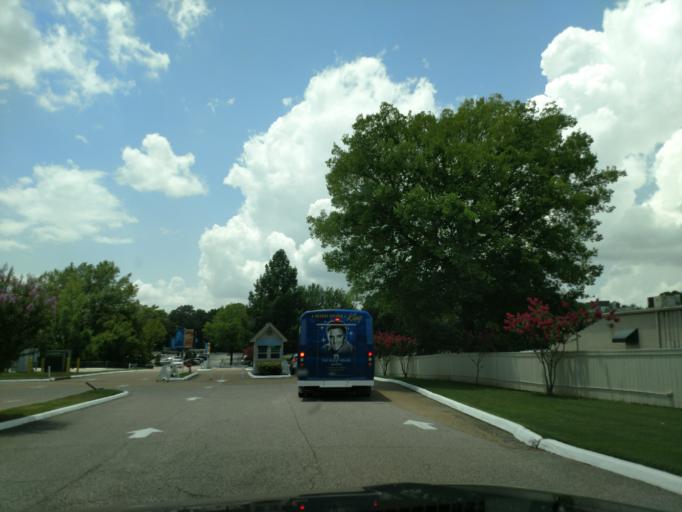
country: US
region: Tennessee
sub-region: Shelby County
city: New South Memphis
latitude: 35.0478
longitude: -90.0254
